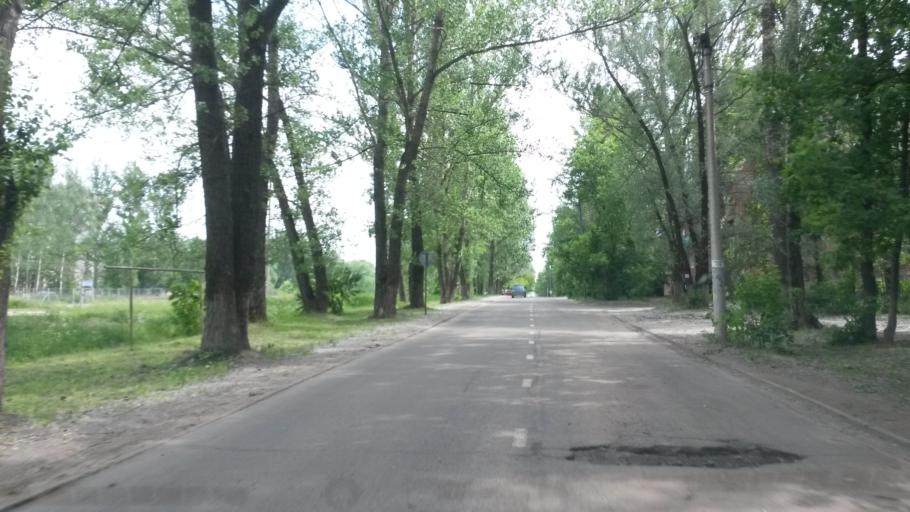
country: RU
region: Jaroslavl
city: Yaroslavl
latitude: 57.5883
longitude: 39.8351
